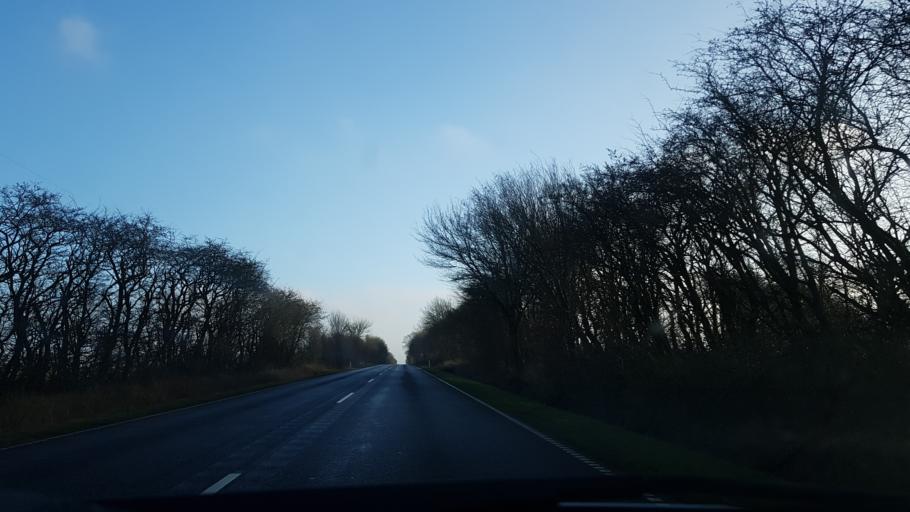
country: DK
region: South Denmark
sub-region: Haderslev Kommune
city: Vojens
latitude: 55.1894
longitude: 9.2162
